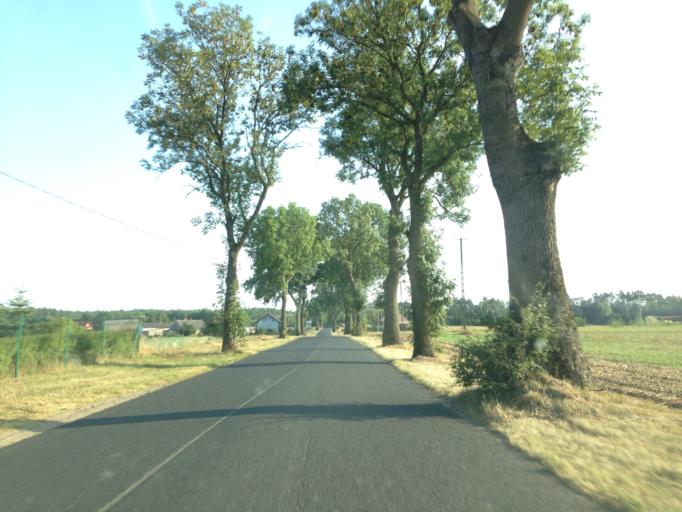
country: PL
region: Kujawsko-Pomorskie
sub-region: Powiat brodnicki
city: Brodnica
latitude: 53.3704
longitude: 19.3752
